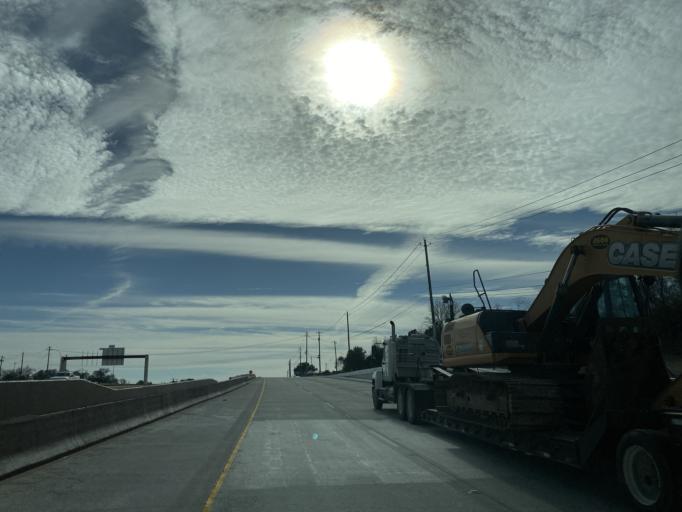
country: US
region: Texas
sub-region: Travis County
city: Austin
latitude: 30.2786
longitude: -97.6678
